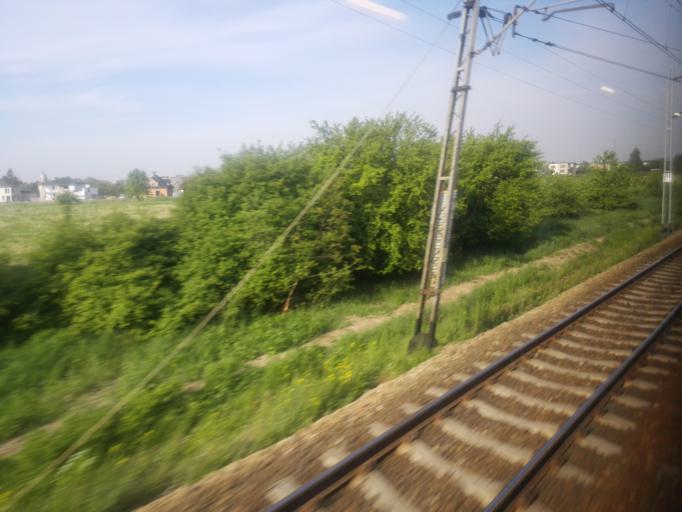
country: PL
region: Greater Poland Voivodeship
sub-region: Powiat wrzesinski
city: Wrzesnia
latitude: 52.3372
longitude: 17.5849
